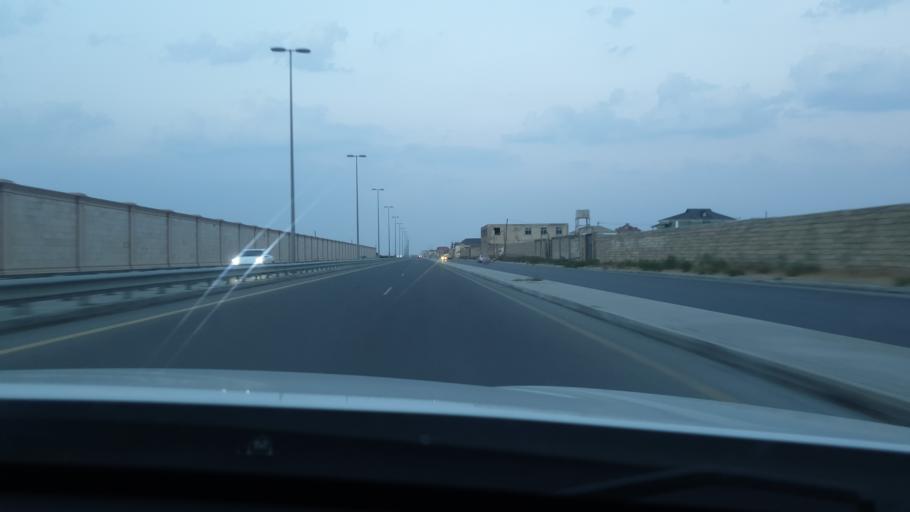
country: AZ
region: Baki
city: Bilajer
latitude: 40.5847
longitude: 50.0247
